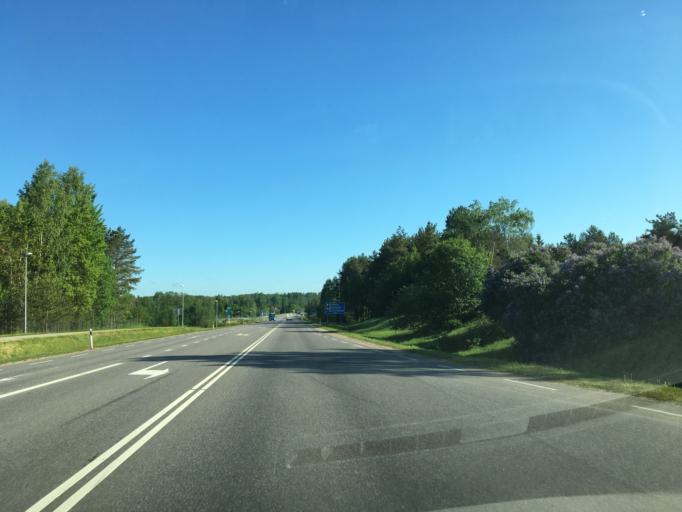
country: EE
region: Tartu
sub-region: Tartu linn
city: Tartu
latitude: 58.4552
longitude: 26.6736
